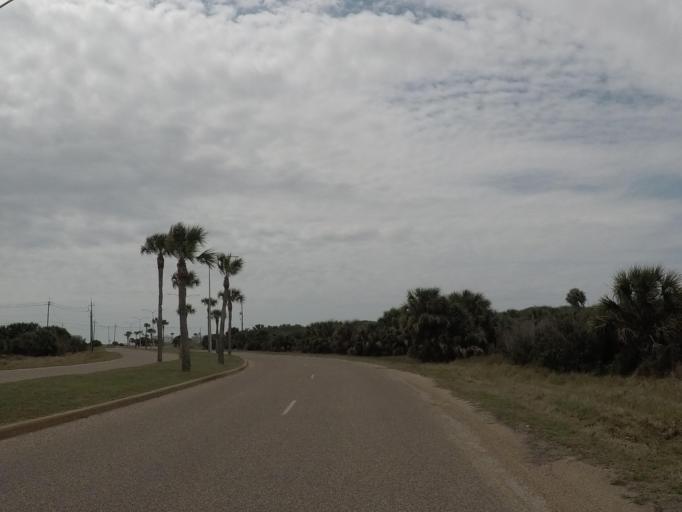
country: US
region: Texas
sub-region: Galveston County
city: Galveston
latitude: 29.3172
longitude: -94.7569
